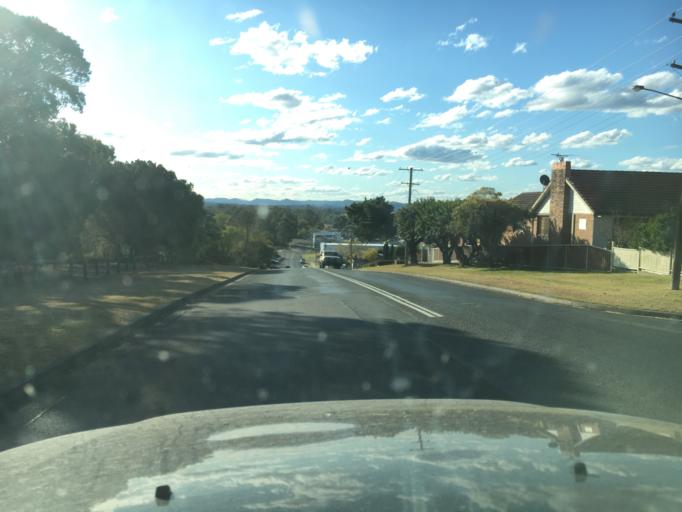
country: AU
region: New South Wales
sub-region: Maitland Municipality
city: East Maitland
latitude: -32.7507
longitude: 151.5808
